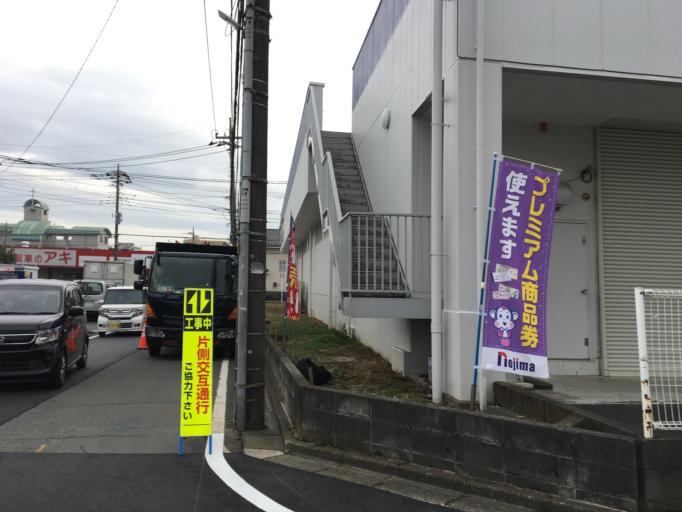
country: JP
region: Saitama
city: Tokorozawa
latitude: 35.7964
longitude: 139.5096
